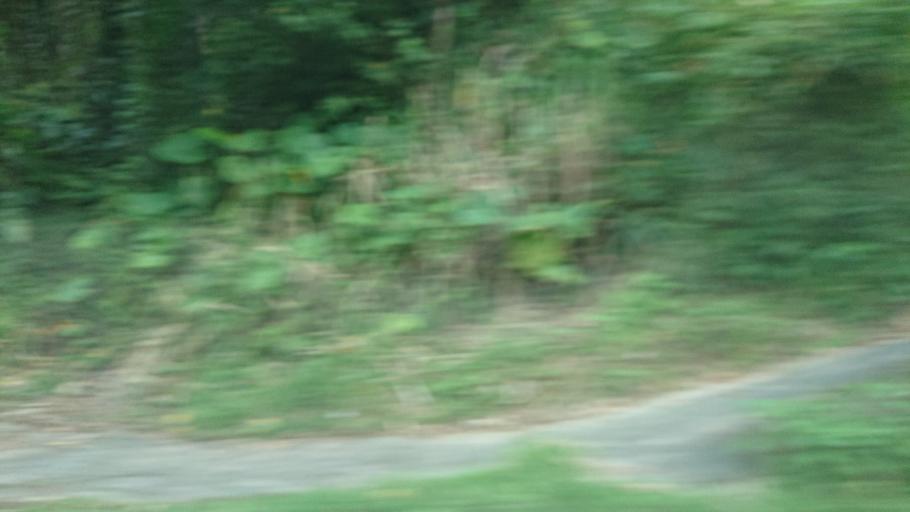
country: TW
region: Taiwan
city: Daxi
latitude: 24.8906
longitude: 121.3768
